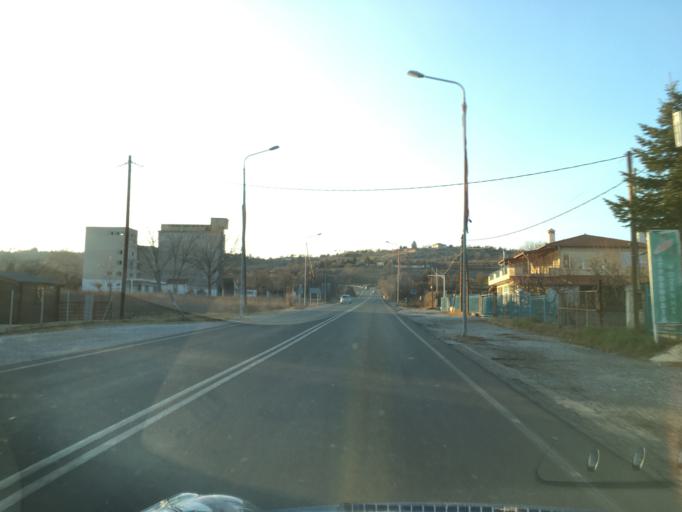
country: GR
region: West Macedonia
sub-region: Nomos Kozanis
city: Kozani
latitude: 40.2873
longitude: 21.7770
